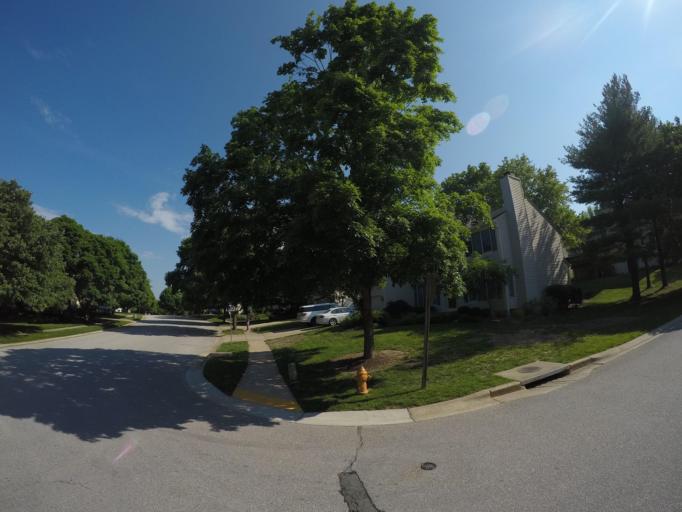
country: US
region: Maryland
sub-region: Howard County
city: Riverside
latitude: 39.1945
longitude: -76.9115
